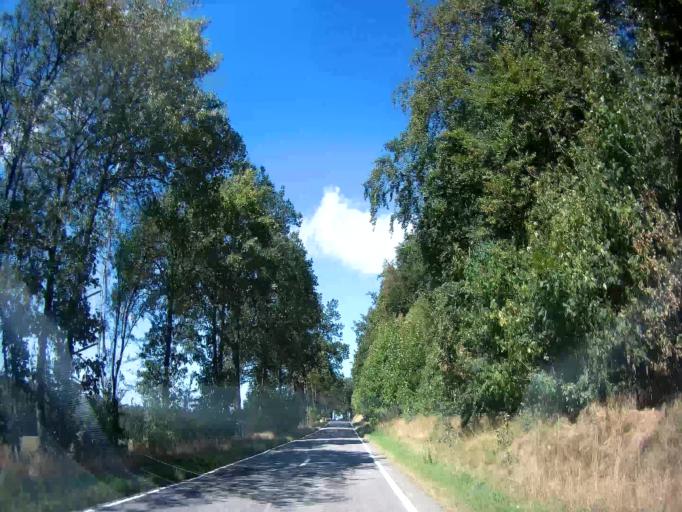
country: BE
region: Wallonia
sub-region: Province du Luxembourg
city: La Roche-en-Ardenne
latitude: 50.1601
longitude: 5.6046
